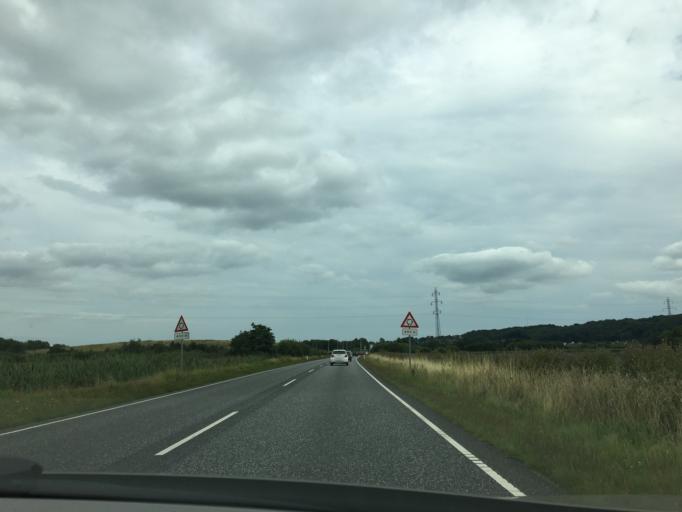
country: DK
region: South Denmark
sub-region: Vejle Kommune
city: Vejle
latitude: 55.7073
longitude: 9.4889
